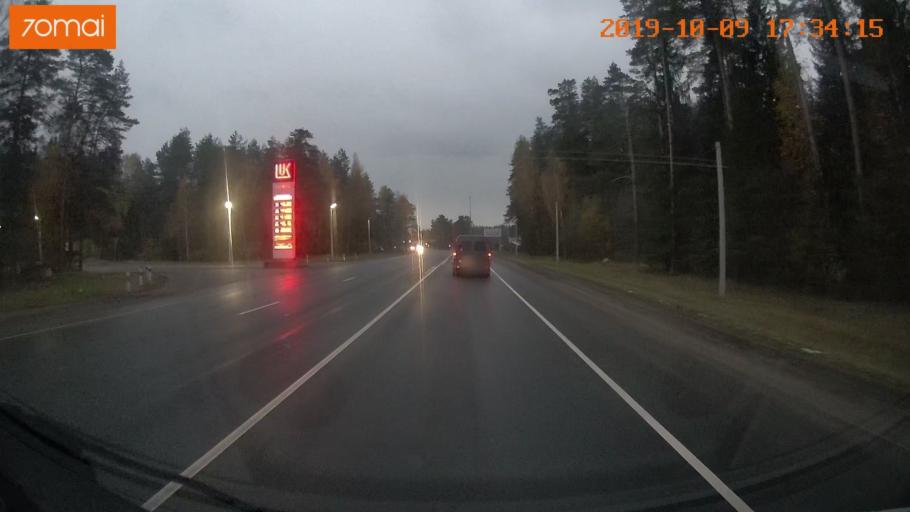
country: RU
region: Ivanovo
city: Bogorodskoye
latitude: 57.1084
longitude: 41.0134
